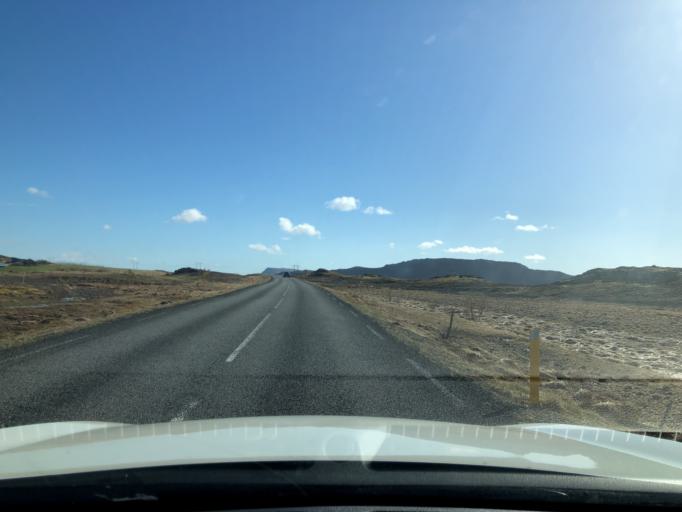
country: IS
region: West
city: Borgarnes
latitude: 64.5597
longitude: -21.7222
